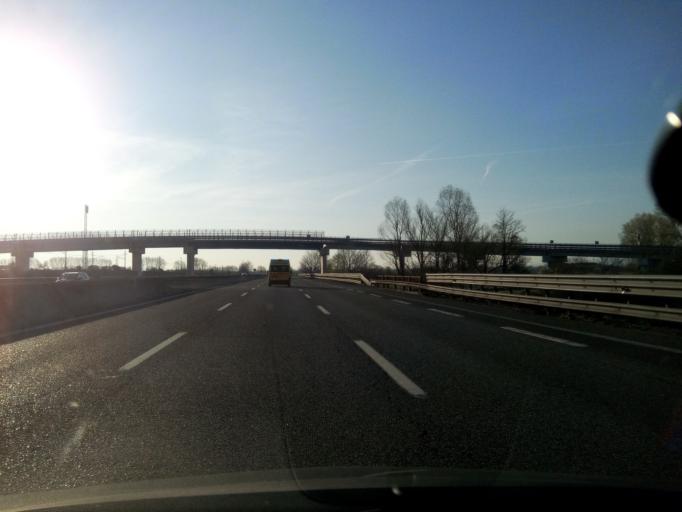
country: IT
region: Emilia-Romagna
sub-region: Provincia di Piacenza
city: Alseno
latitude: 44.9303
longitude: 9.9784
